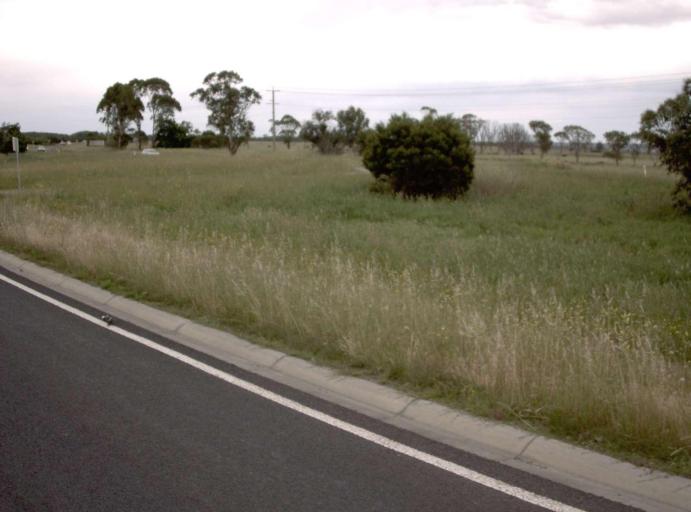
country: AU
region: Victoria
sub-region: Cardinia
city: Koo-Wee-Rup
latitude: -38.2567
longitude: 145.5502
